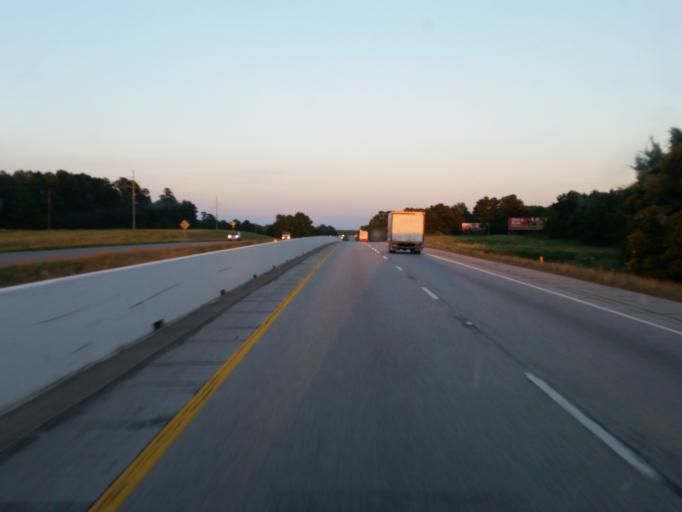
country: US
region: Texas
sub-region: Smith County
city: Hideaway
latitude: 32.4782
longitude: -95.4852
